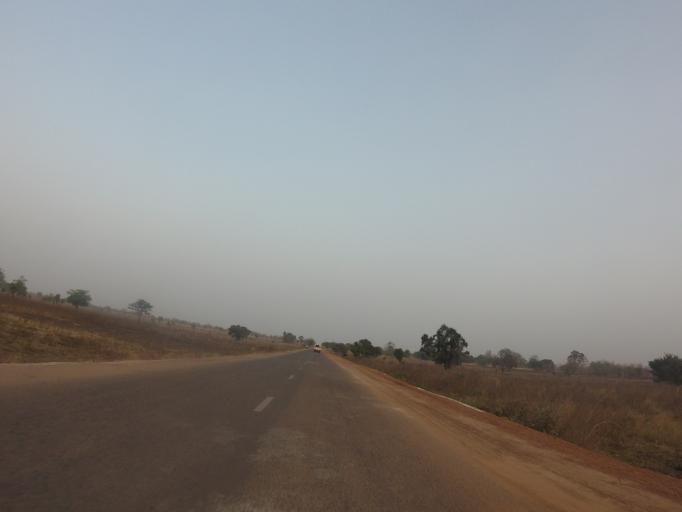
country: GH
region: Northern
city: Tamale
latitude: 9.4414
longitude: -1.1038
